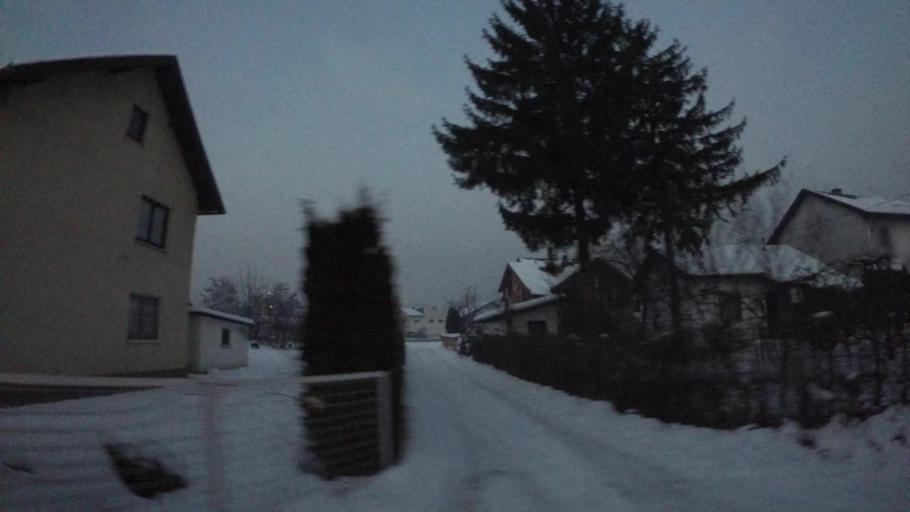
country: BA
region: Federation of Bosnia and Herzegovina
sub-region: Kanton Sarajevo
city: Sarajevo
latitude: 43.8362
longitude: 18.3197
